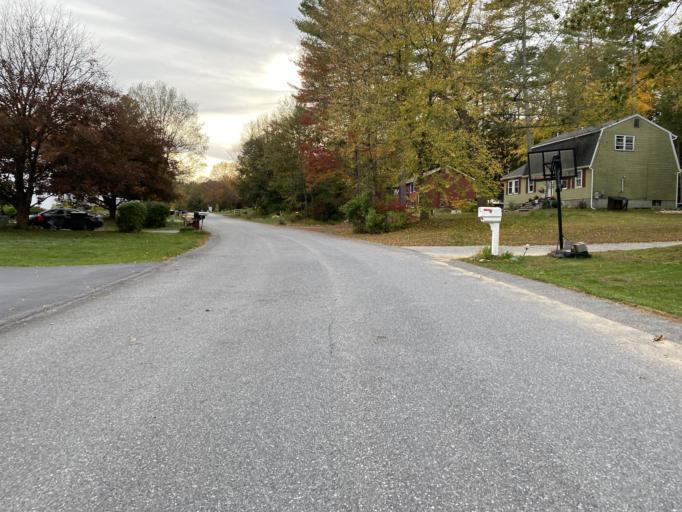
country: US
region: New York
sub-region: Saratoga County
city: Milton
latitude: 43.0984
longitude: -73.9042
